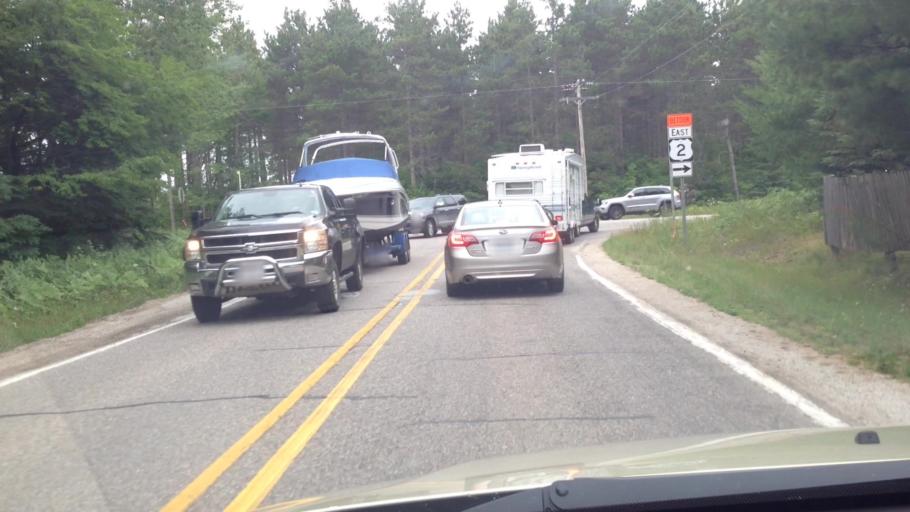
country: US
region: Michigan
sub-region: Mackinac County
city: Saint Ignace
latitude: 46.0563
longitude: -85.1508
